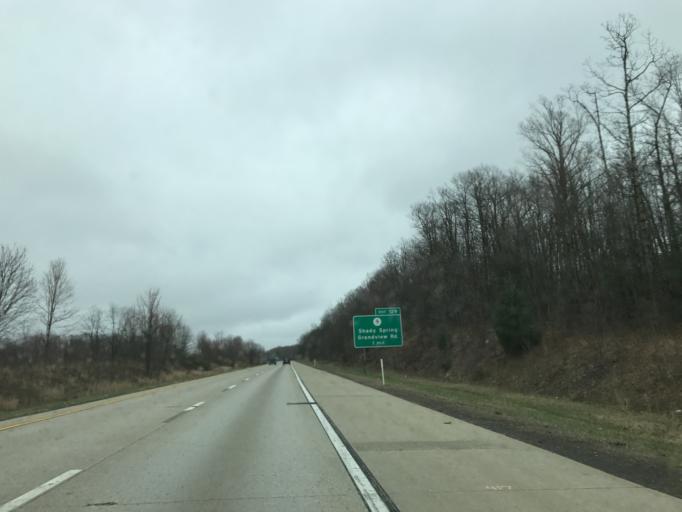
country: US
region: West Virginia
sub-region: Raleigh County
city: Daniels
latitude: 37.7743
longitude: -81.0911
